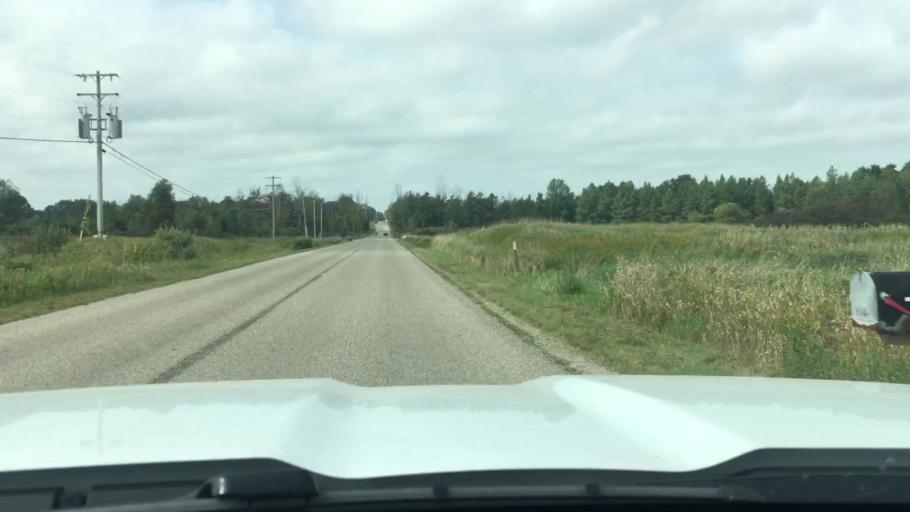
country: US
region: Michigan
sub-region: Eaton County
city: Potterville
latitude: 42.6256
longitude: -84.6970
